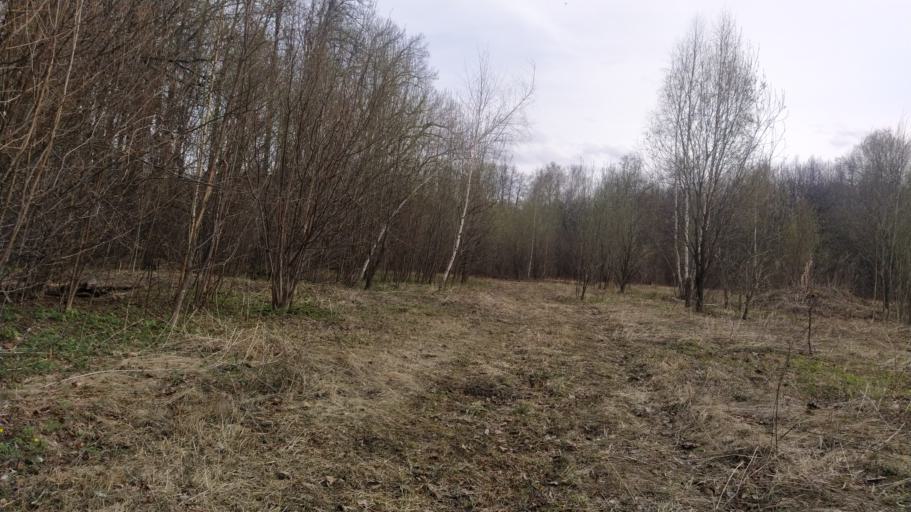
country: RU
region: Chuvashia
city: Novyye Lapsary
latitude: 56.1400
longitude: 47.1233
